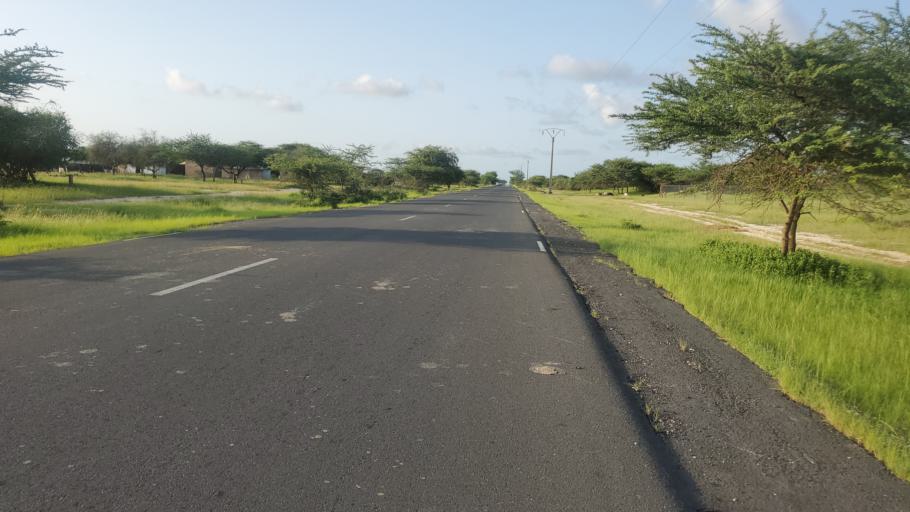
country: SN
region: Saint-Louis
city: Saint-Louis
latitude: 16.1691
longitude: -16.4098
